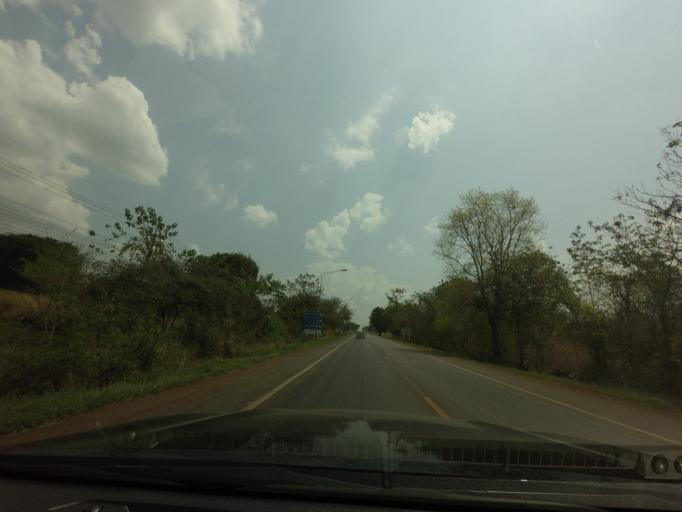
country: TH
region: Kanchanaburi
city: Sai Yok
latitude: 14.1323
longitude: 99.1595
